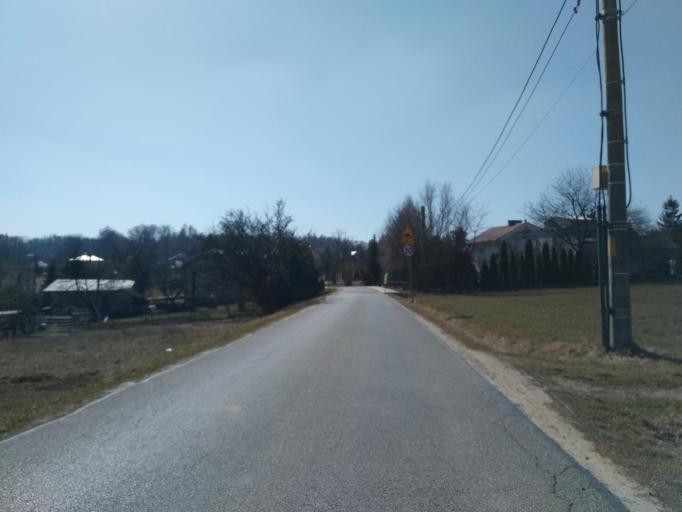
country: PL
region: Subcarpathian Voivodeship
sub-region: Powiat strzyzowski
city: Czudec
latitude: 49.9774
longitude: 21.8380
